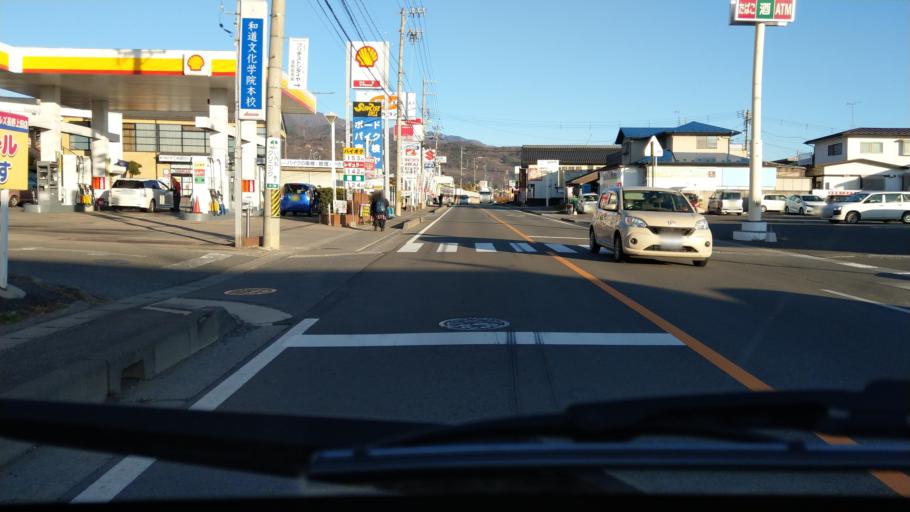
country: JP
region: Nagano
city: Ueda
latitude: 36.4015
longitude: 138.2863
